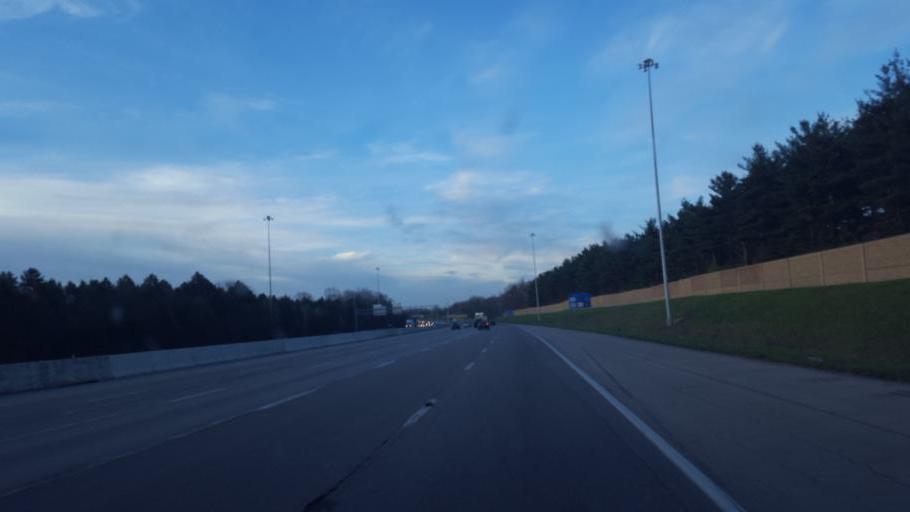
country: US
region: Ohio
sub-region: Franklin County
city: Westerville
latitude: 40.1148
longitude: -82.9747
